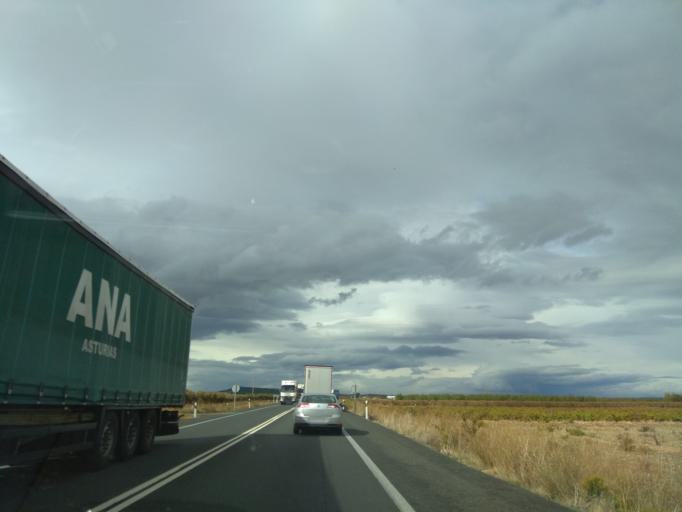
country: ES
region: La Rioja
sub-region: Provincia de La Rioja
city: Aldeanueva de Ebro
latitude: 42.2562
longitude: -1.9080
